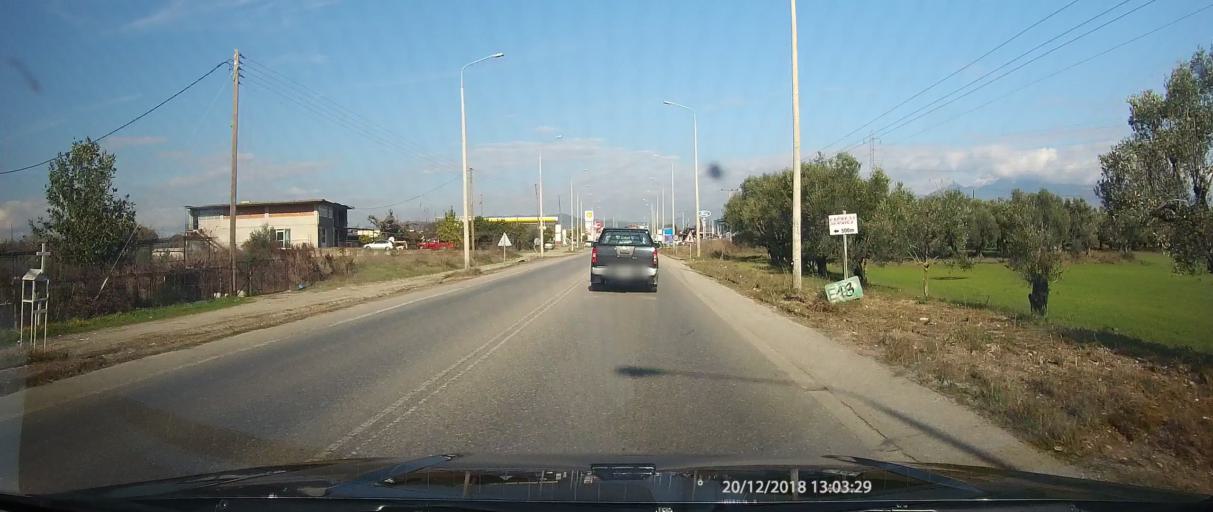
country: GR
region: West Greece
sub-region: Nomos Aitolias kai Akarnanias
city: Panaitolion
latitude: 38.5817
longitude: 21.4268
